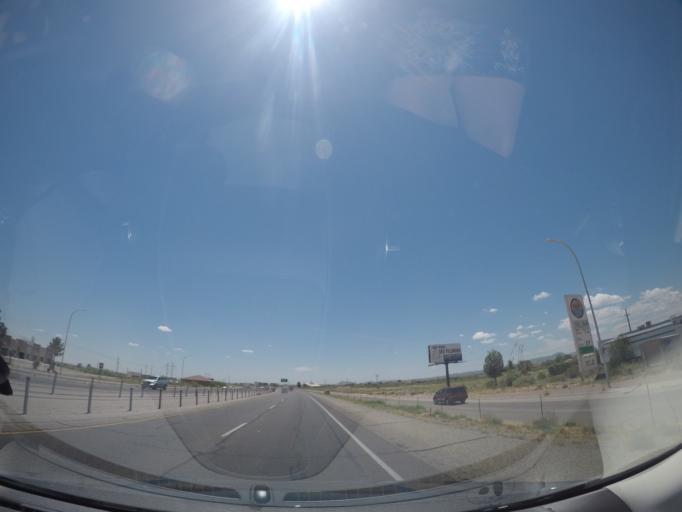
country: US
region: New Mexico
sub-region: Dona Ana County
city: Las Cruces
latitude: 32.3802
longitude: -106.7296
